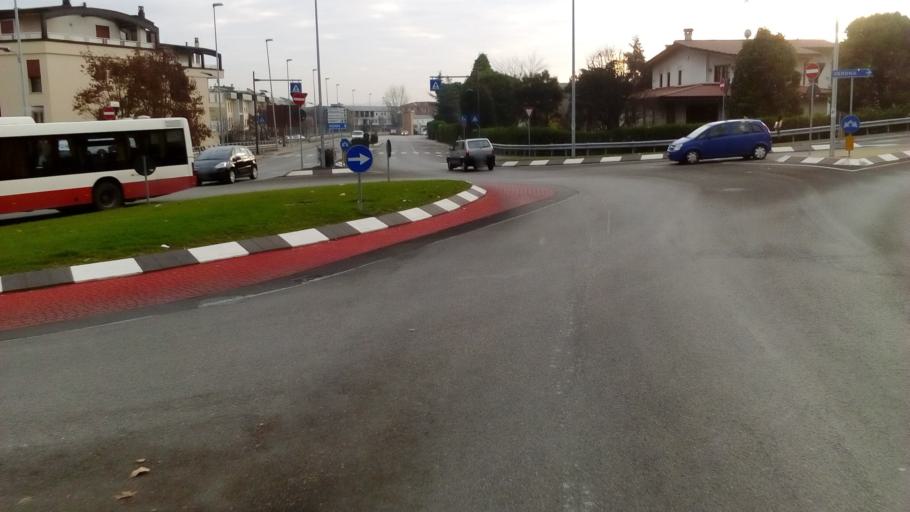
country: IT
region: Veneto
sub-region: Provincia di Vicenza
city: Arzignano
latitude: 45.5171
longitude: 11.3338
